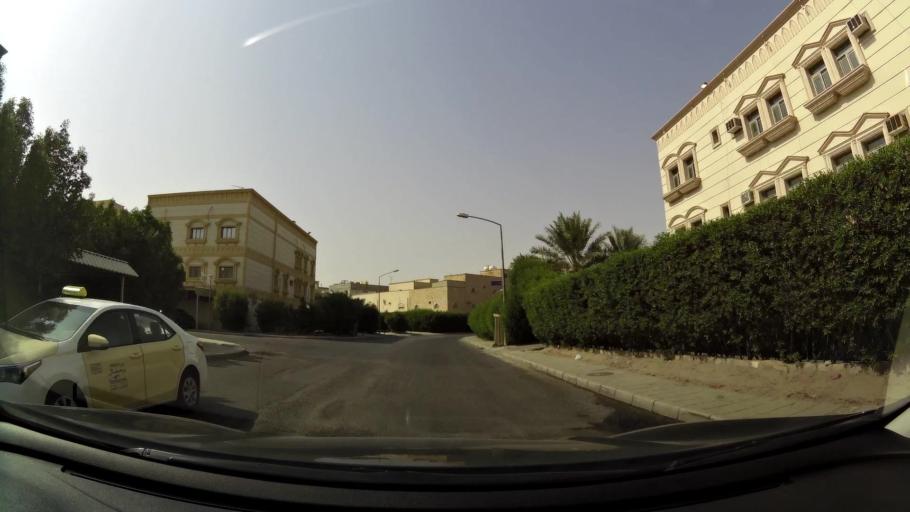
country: KW
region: Muhafazat al Jahra'
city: Al Jahra'
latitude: 29.3250
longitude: 47.6517
